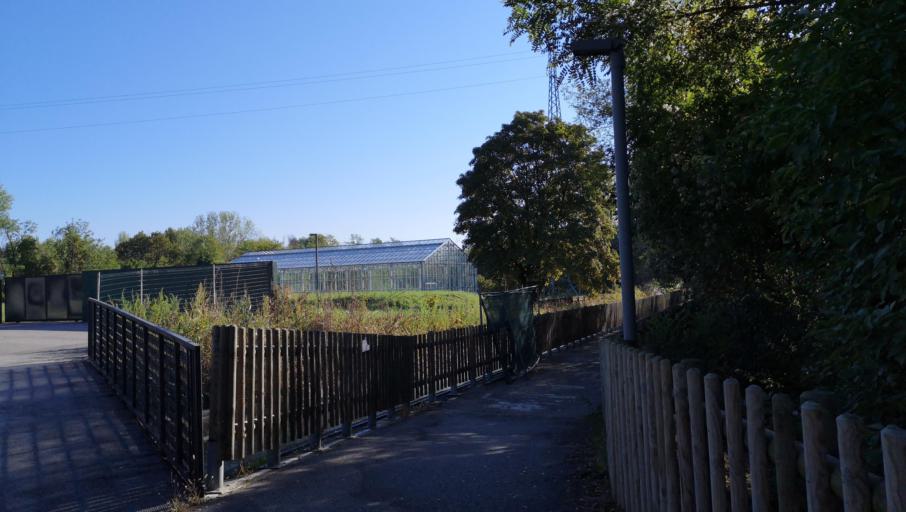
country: IT
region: Friuli Venezia Giulia
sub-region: Provincia di Udine
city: Colugna
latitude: 46.0887
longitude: 13.1883
